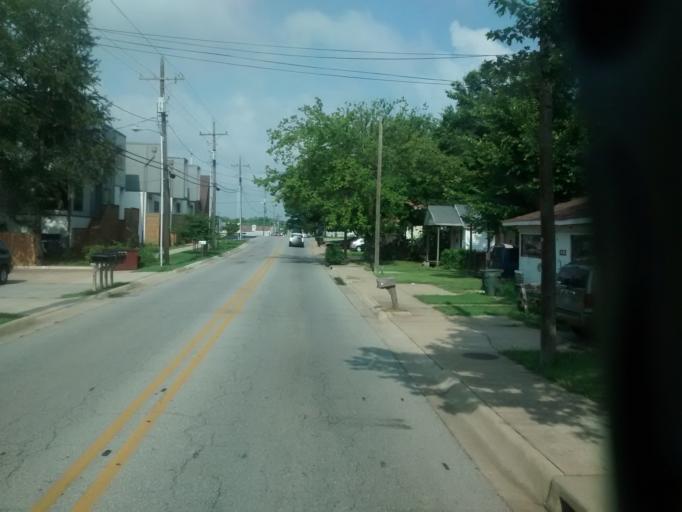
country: US
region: Arkansas
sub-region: Washington County
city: Fayetteville
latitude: 36.0564
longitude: -94.1610
